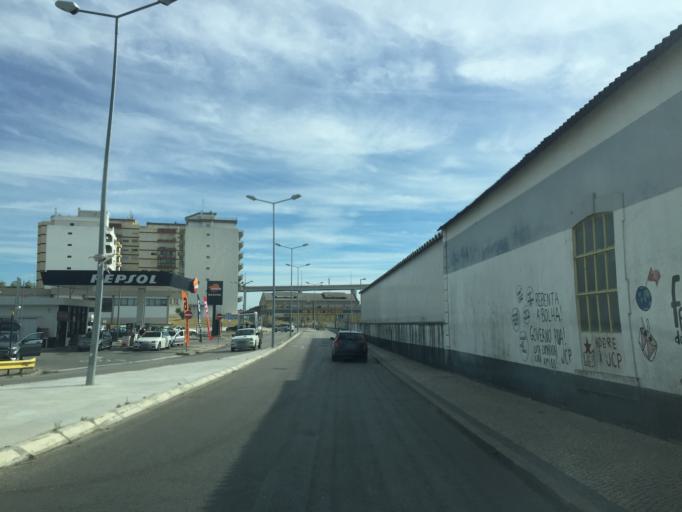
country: PT
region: Coimbra
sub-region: Figueira da Foz
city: Figueira da Foz
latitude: 40.1481
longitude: -8.8494
